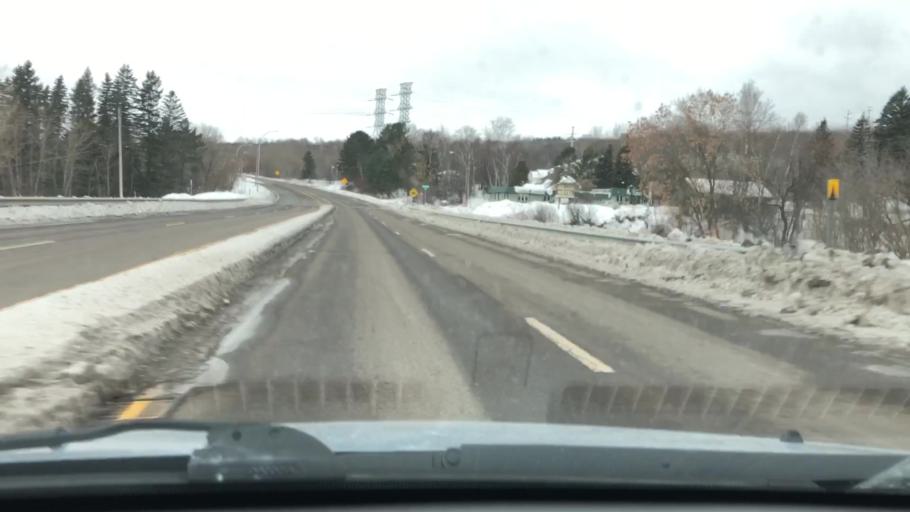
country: US
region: Minnesota
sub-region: Saint Louis County
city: Proctor
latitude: 46.7410
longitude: -92.1799
